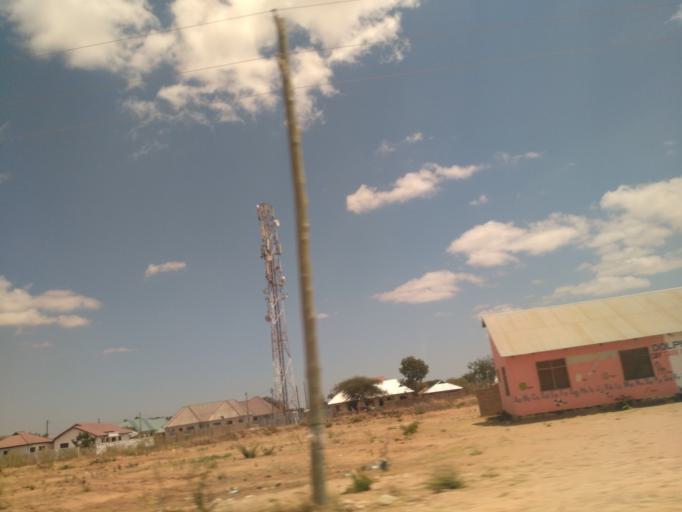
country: TZ
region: Dodoma
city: Kisasa
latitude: -6.1657
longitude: 35.7911
